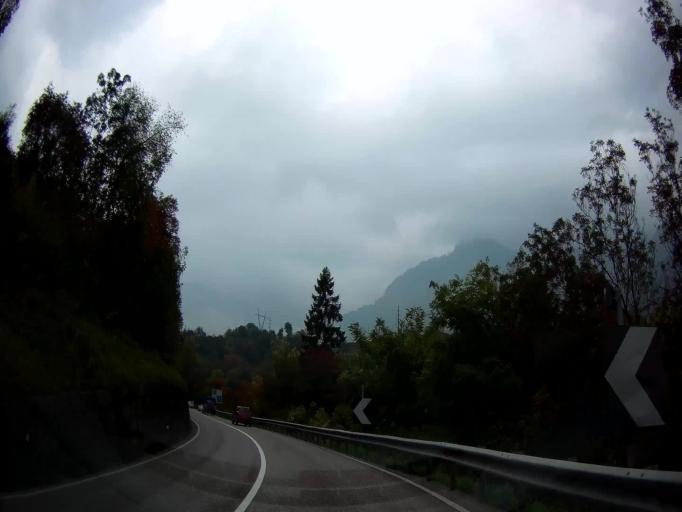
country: IT
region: Trentino-Alto Adige
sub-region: Bolzano
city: Parcines
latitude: 46.6812
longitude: 11.0960
